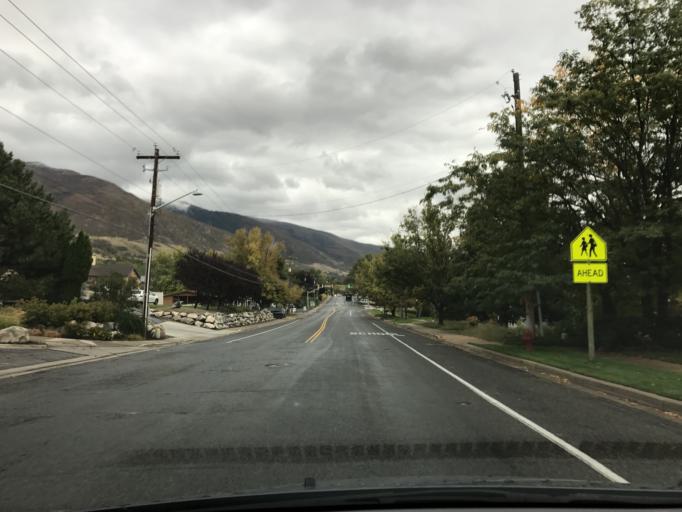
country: US
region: Utah
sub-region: Davis County
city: Farmington
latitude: 41.0022
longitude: -111.9019
